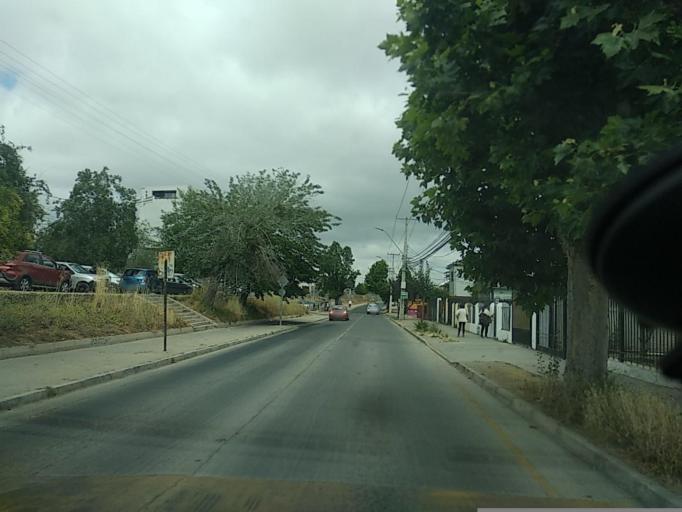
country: CL
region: Valparaiso
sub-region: Provincia de Marga Marga
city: Villa Alemana
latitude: -33.0421
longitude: -71.3741
